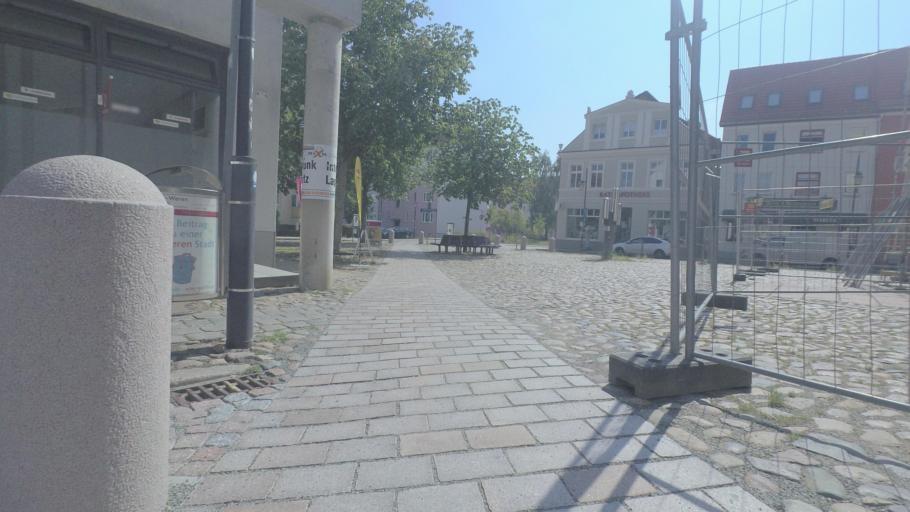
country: DE
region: Mecklenburg-Vorpommern
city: Malchin
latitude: 53.7394
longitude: 12.7631
